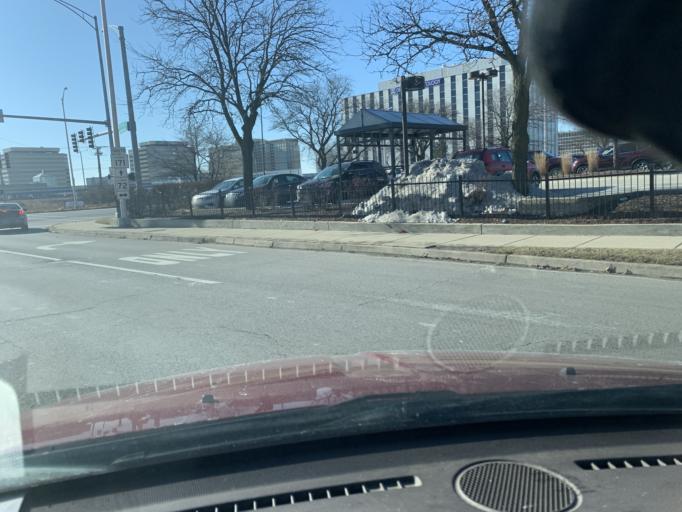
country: US
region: Illinois
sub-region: Cook County
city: Park Ridge
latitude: 41.9869
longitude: -87.8367
